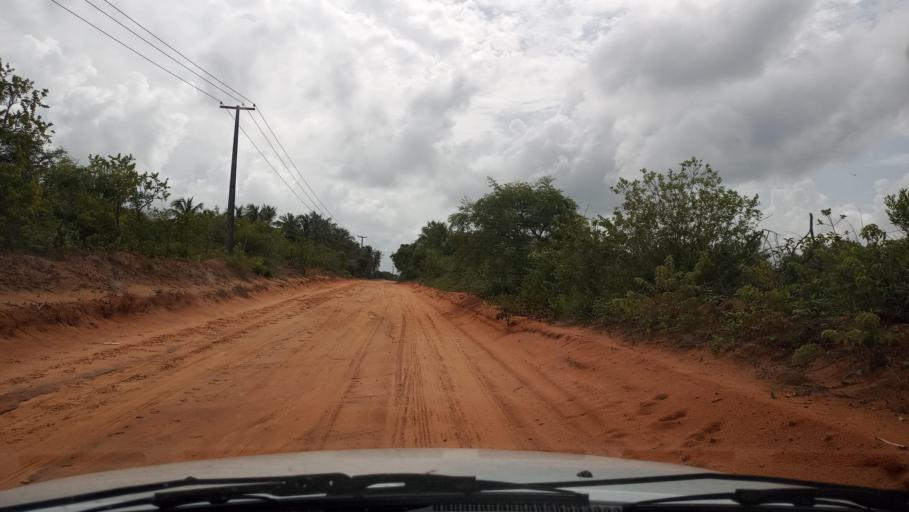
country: BR
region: Rio Grande do Norte
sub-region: Maxaranguape
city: Sao Miguel
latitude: -5.4834
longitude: -35.3170
